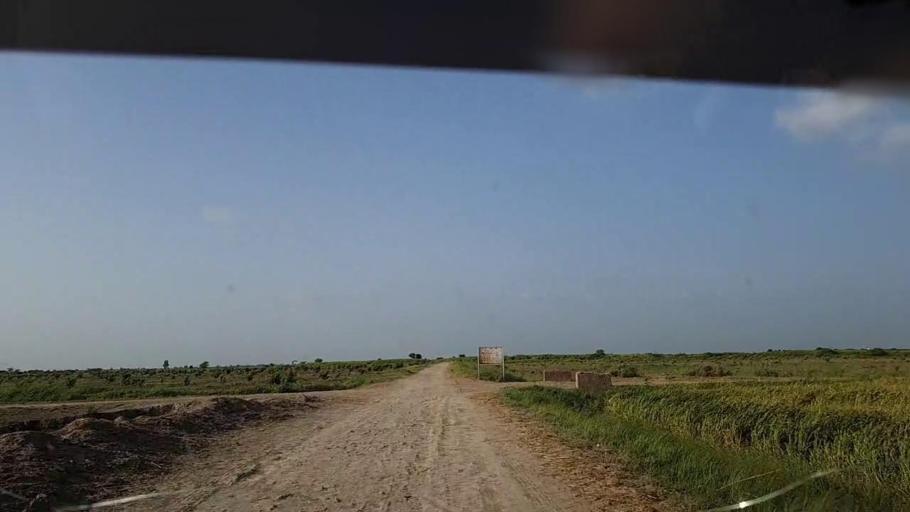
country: PK
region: Sindh
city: Badin
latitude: 24.5636
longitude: 68.8826
